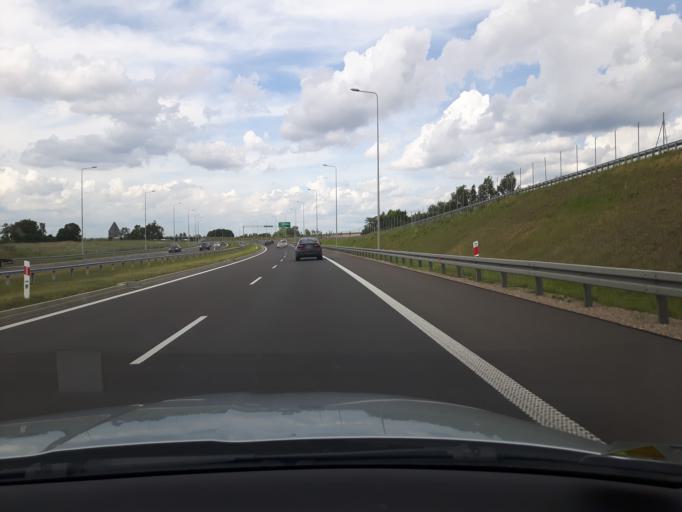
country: PL
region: Warmian-Masurian Voivodeship
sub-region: Powiat nidzicki
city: Nidzica
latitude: 53.3276
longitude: 20.4398
